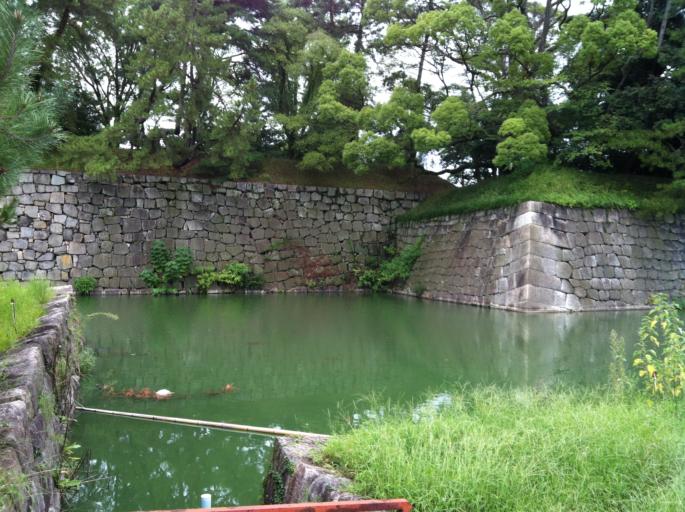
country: JP
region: Kyoto
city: Kyoto
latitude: 35.0122
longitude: 135.7475
